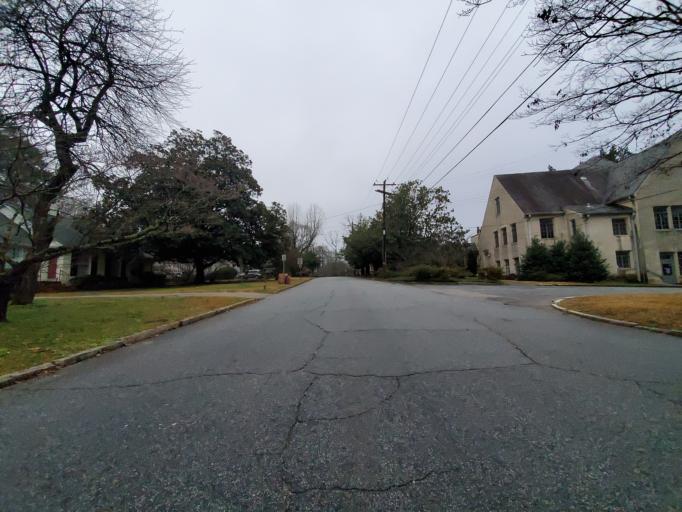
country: US
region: Georgia
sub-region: DeKalb County
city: North Decatur
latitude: 33.7932
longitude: -84.3143
